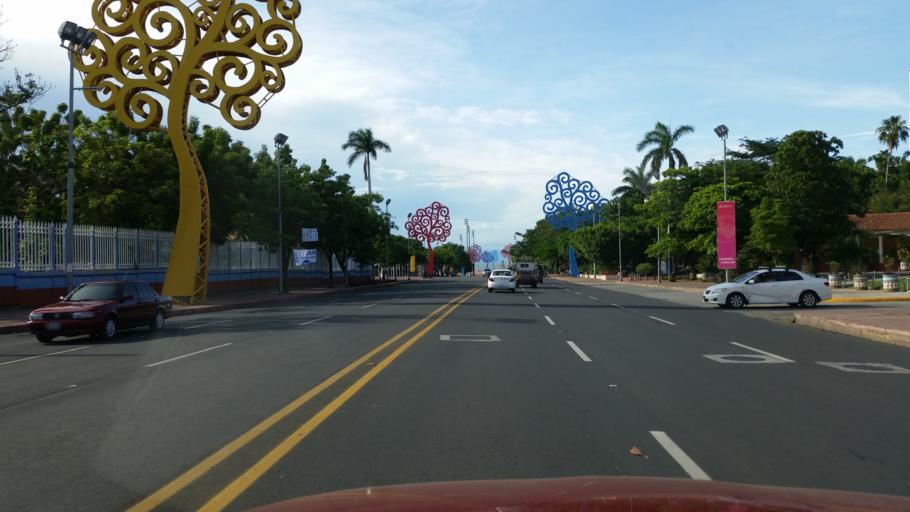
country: NI
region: Managua
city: Managua
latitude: 12.1558
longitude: -86.2736
